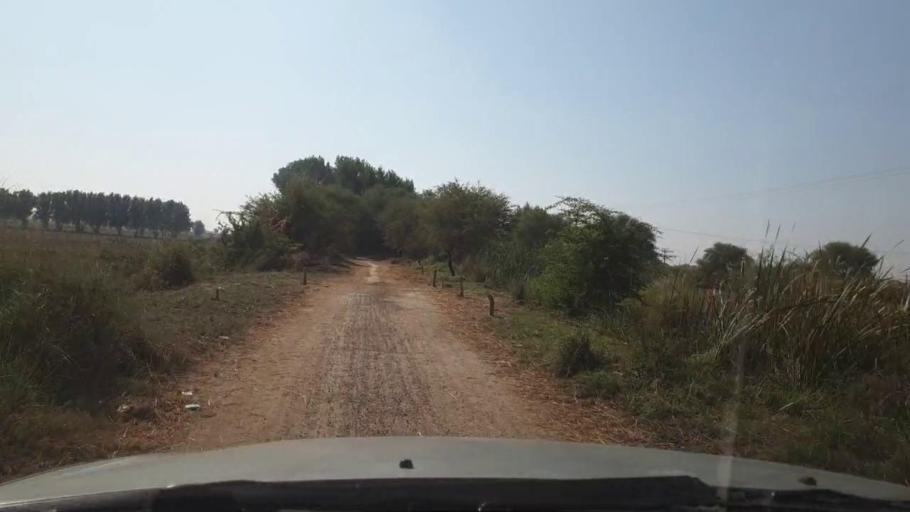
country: PK
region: Sindh
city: Kario
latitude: 24.8878
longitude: 68.5589
